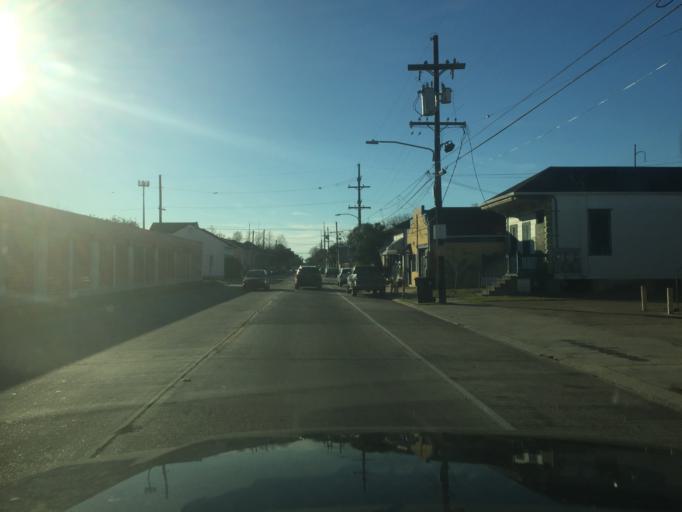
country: US
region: Louisiana
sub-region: Jefferson Parish
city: Marrero
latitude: 29.9177
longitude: -90.0946
